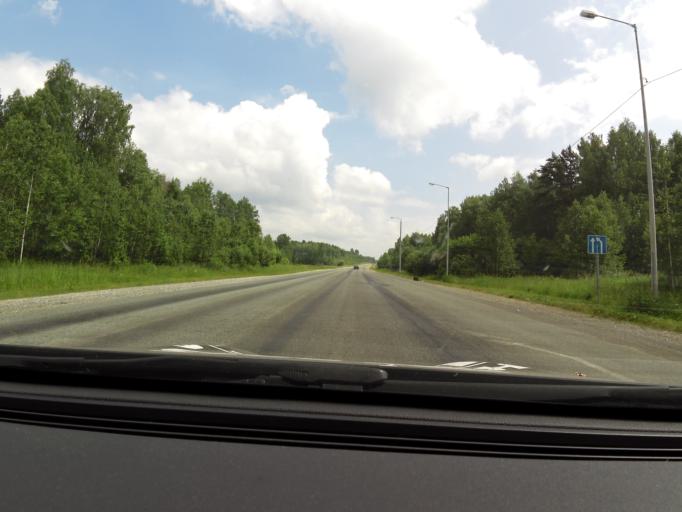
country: RU
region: Sverdlovsk
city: Achit
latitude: 56.8530
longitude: 57.7199
